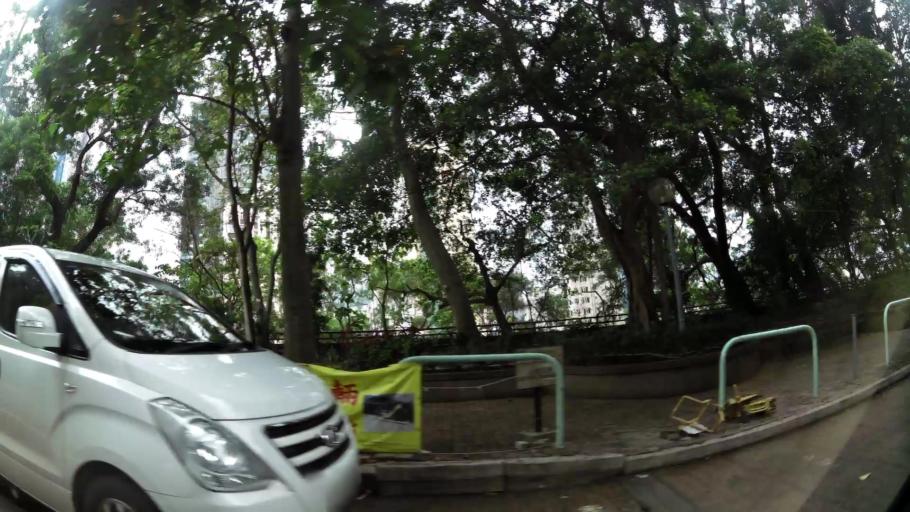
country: HK
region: Central and Western
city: Central
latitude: 22.2432
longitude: 114.1563
